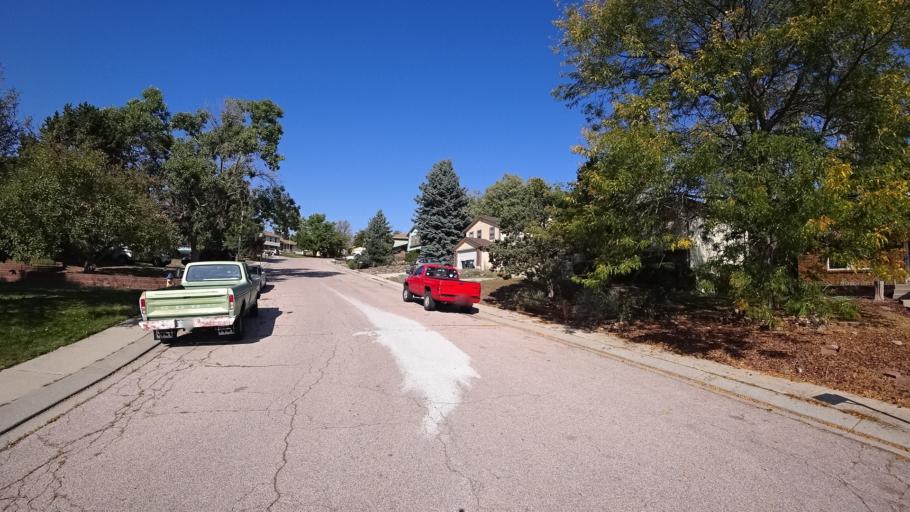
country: US
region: Colorado
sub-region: El Paso County
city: Cimarron Hills
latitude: 38.8863
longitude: -104.7242
